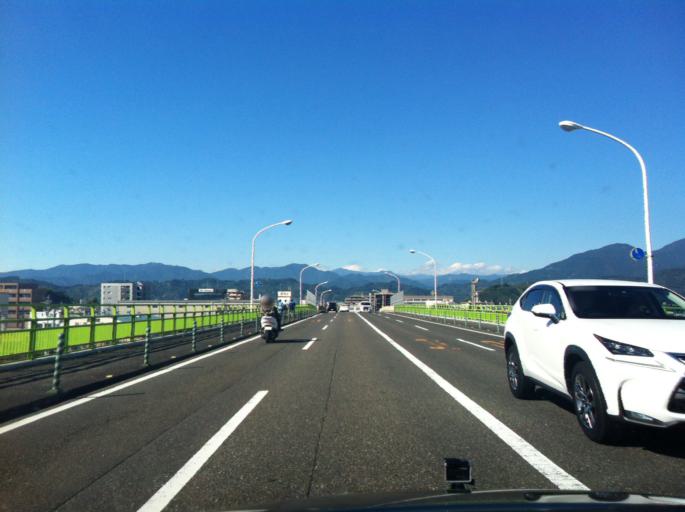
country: JP
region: Shizuoka
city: Shizuoka-shi
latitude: 34.9882
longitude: 138.4212
